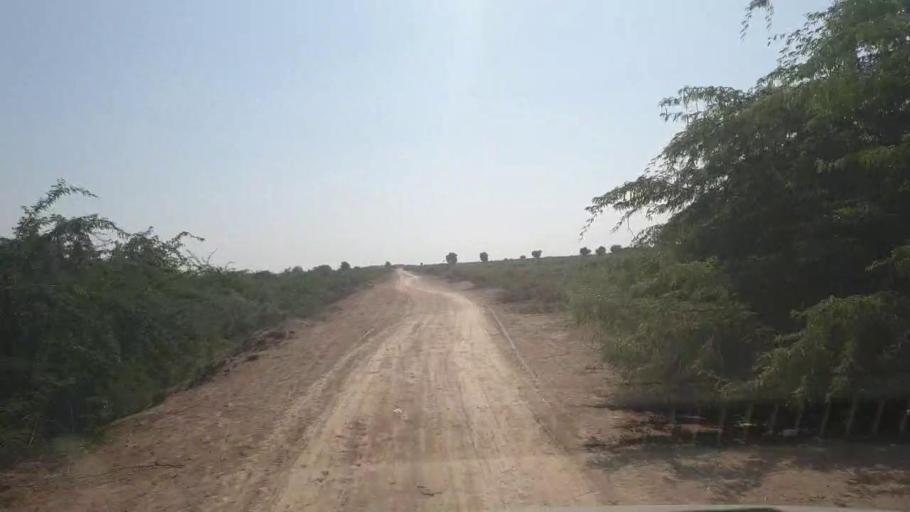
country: PK
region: Sindh
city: Tando Bago
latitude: 24.8825
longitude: 69.1644
